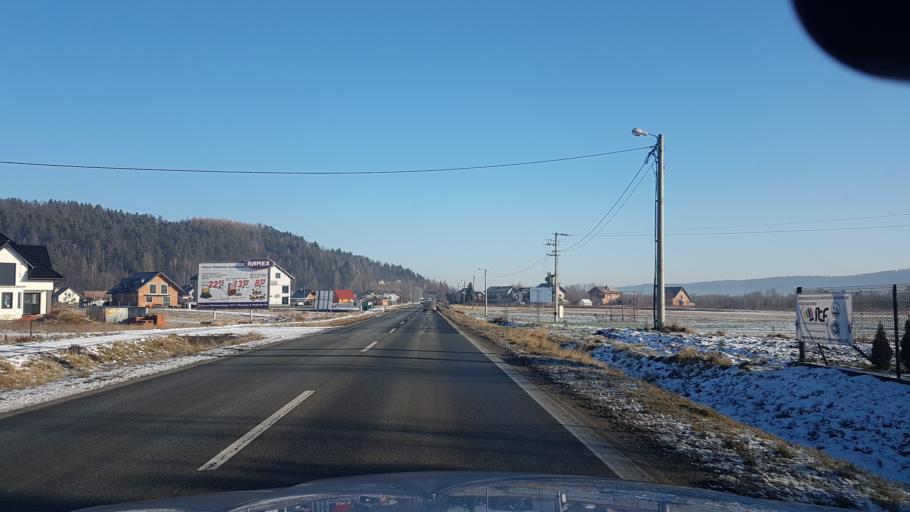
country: PL
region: Lesser Poland Voivodeship
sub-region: Powiat nowosadecki
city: Olszana
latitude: 49.5377
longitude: 20.5512
